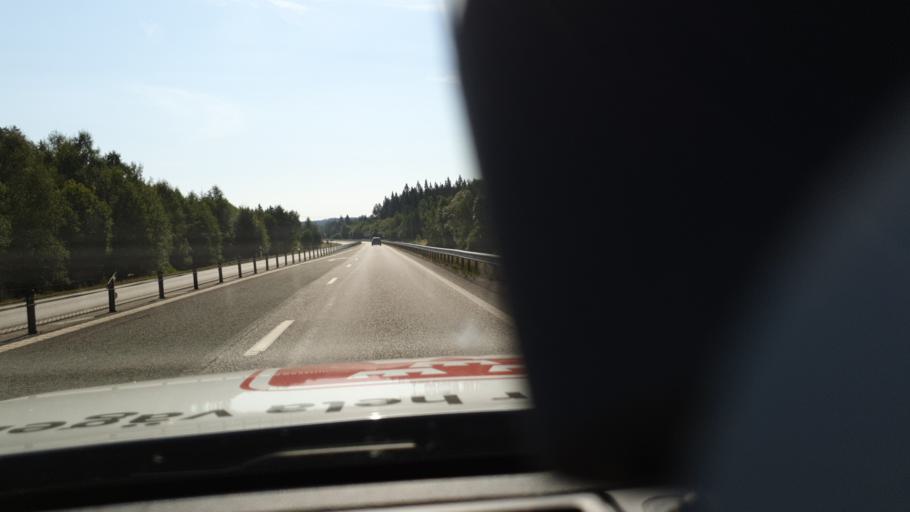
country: SE
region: Joenkoeping
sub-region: Nassjo Kommun
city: Malmback
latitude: 57.6801
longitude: 14.4772
